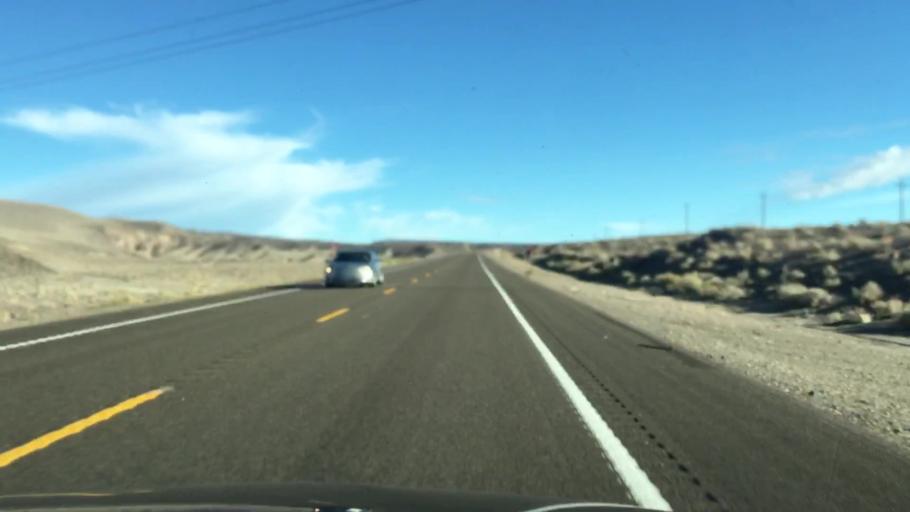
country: US
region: Nevada
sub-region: Mineral County
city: Hawthorne
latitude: 38.2377
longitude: -118.0324
